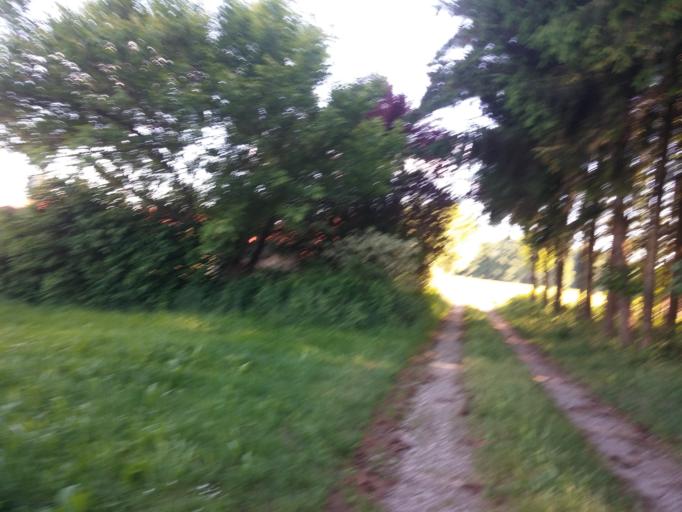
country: DE
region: Baden-Wuerttemberg
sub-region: Tuebingen Region
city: Berkheim
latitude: 48.0368
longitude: 10.0783
